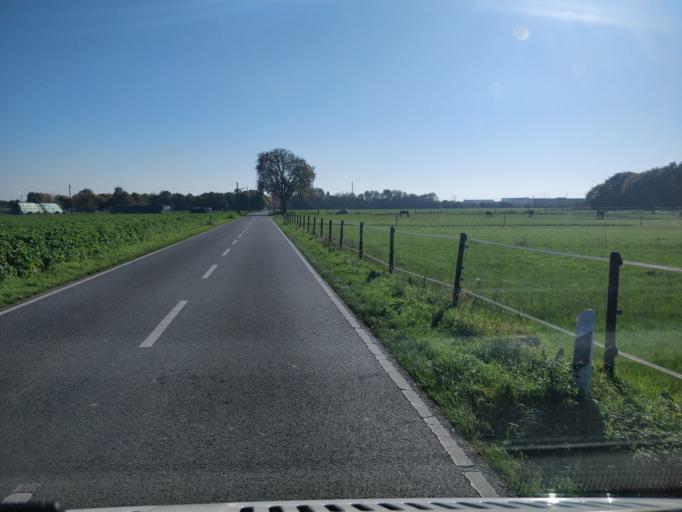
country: DE
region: North Rhine-Westphalia
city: Monheim am Rhein
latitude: 51.0491
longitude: 6.9104
